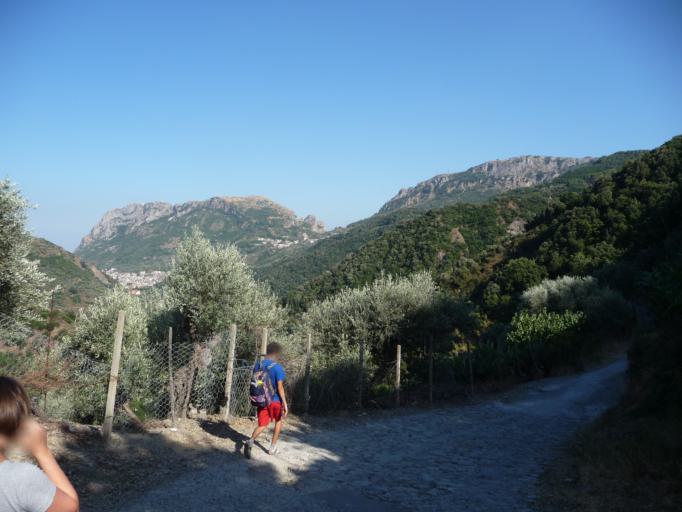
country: IT
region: Calabria
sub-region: Provincia di Reggio Calabria
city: Bivongi
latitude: 38.4874
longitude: 16.4247
